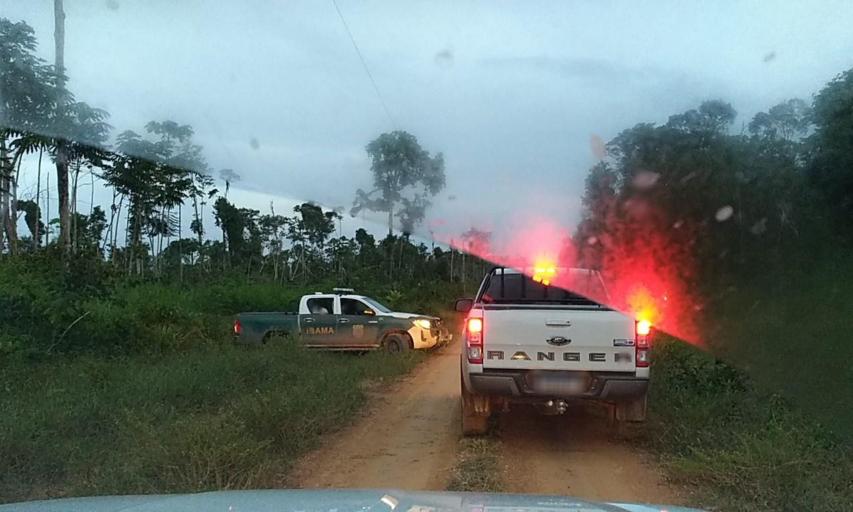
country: BR
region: Para
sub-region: Senador Jose Porfirio
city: Senador Jose Porfirio
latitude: -2.8934
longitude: -51.6890
